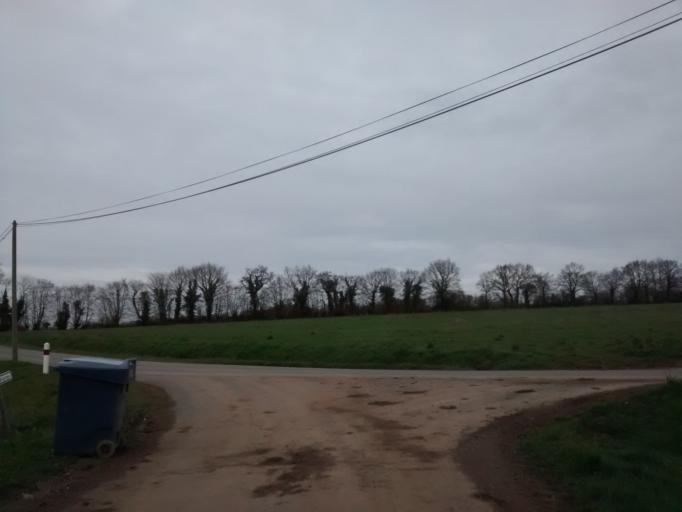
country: FR
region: Brittany
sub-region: Departement d'Ille-et-Vilaine
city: Liffre
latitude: 48.2123
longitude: -1.4790
